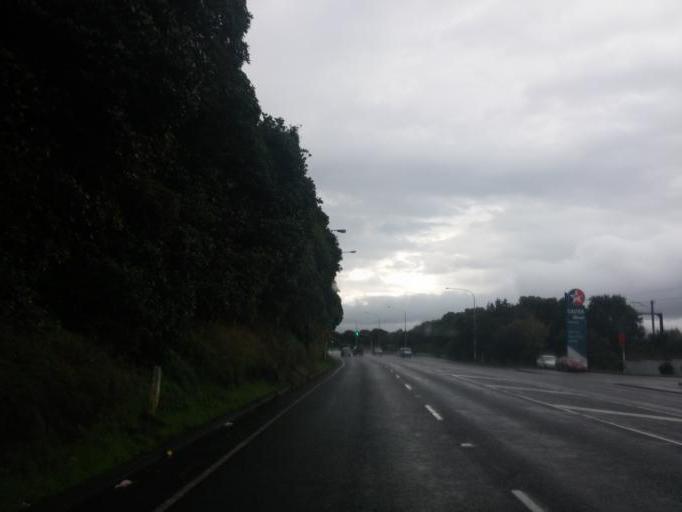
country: NZ
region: Wellington
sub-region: Wellington City
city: Wellington
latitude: -41.2551
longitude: 174.7980
